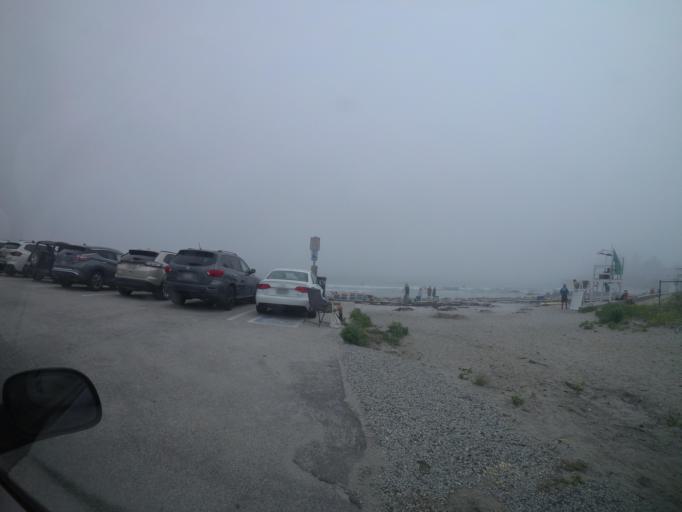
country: US
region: Maine
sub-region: York County
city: Kennebunkport
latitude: 43.3440
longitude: -70.4996
